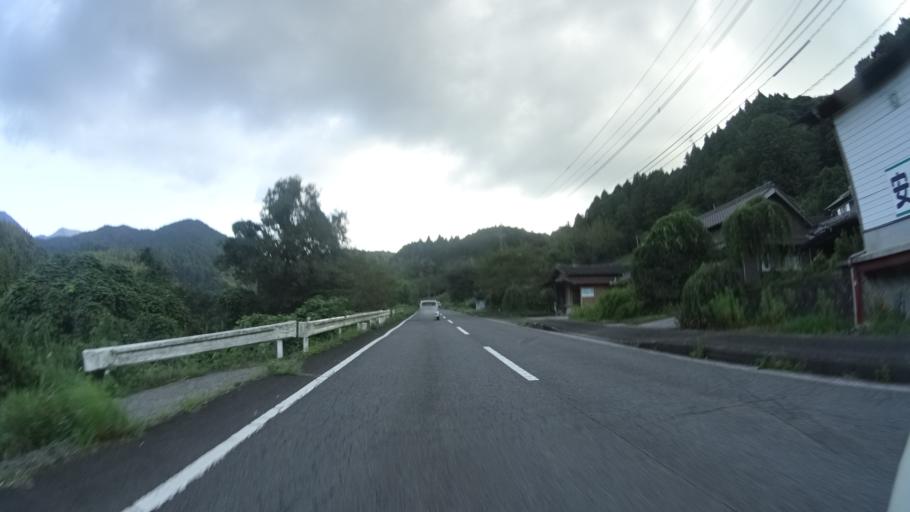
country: JP
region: Oita
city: Beppu
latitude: 33.3420
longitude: 131.3993
